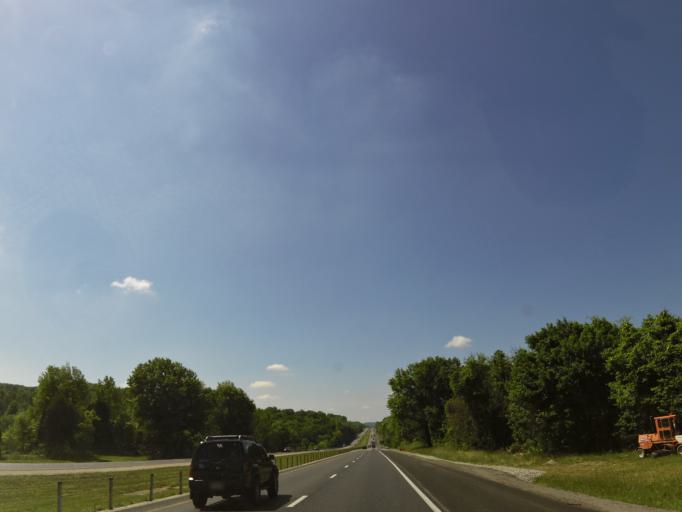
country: US
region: Kentucky
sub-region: Rockcastle County
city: Mount Vernon
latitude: 37.4245
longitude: -84.3432
